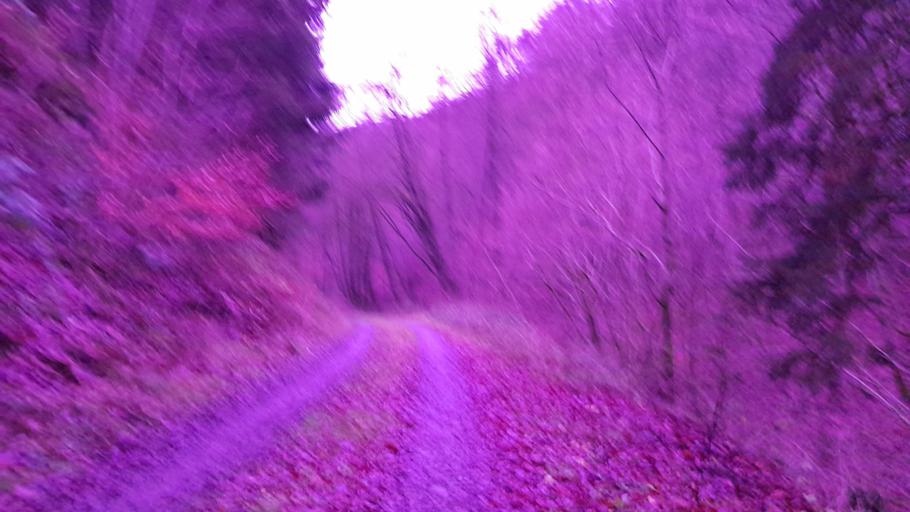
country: DE
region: Rheinland-Pfalz
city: Dasburg
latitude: 50.0768
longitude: 6.1040
